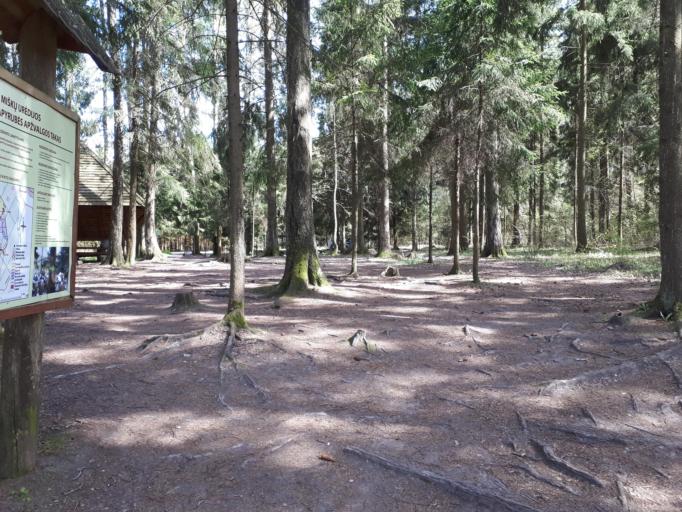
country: LT
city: Ramuciai
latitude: 54.8478
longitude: 24.0796
